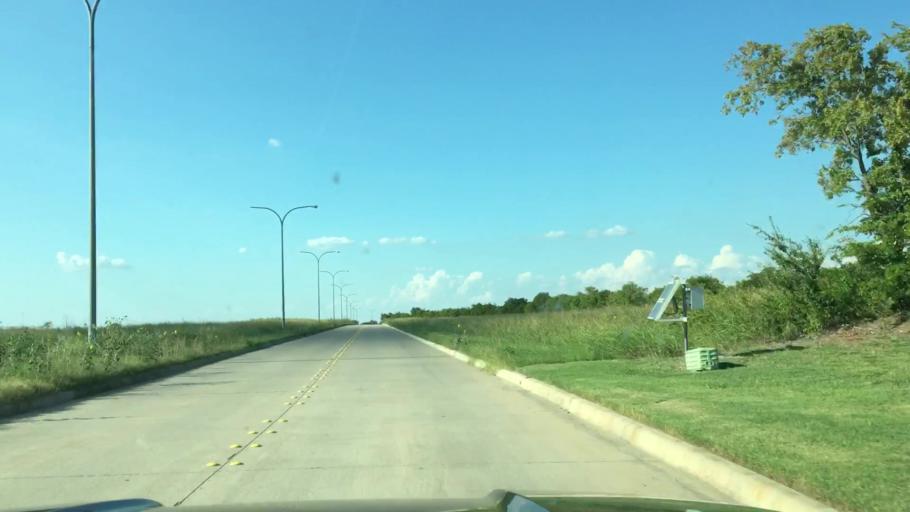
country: US
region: Texas
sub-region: Tarrant County
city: Haslet
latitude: 33.0001
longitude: -97.3588
